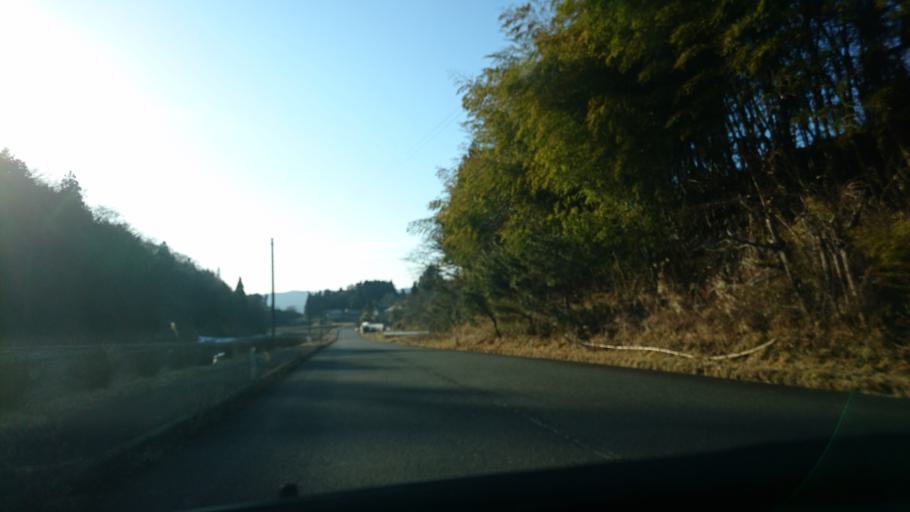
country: JP
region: Iwate
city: Ichinoseki
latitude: 38.9197
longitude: 141.3730
